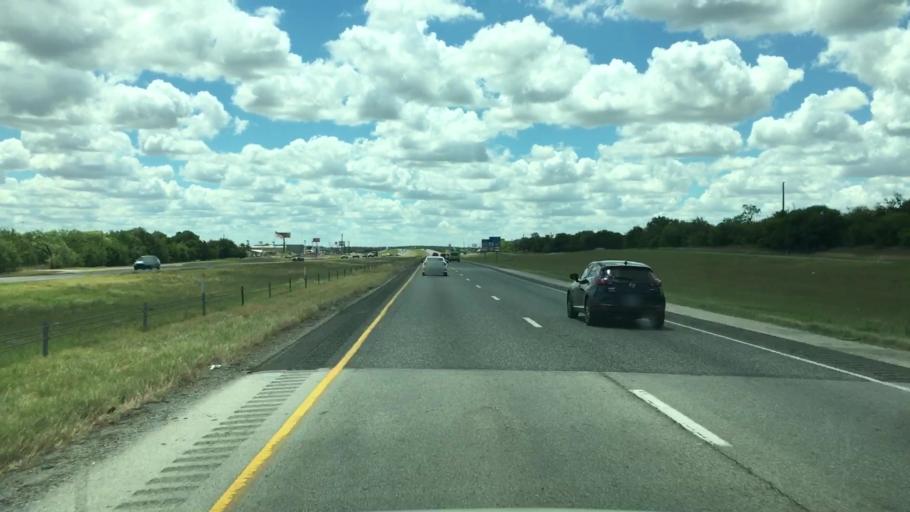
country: US
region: Texas
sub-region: Bexar County
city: Elmendorf
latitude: 29.2291
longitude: -98.4067
